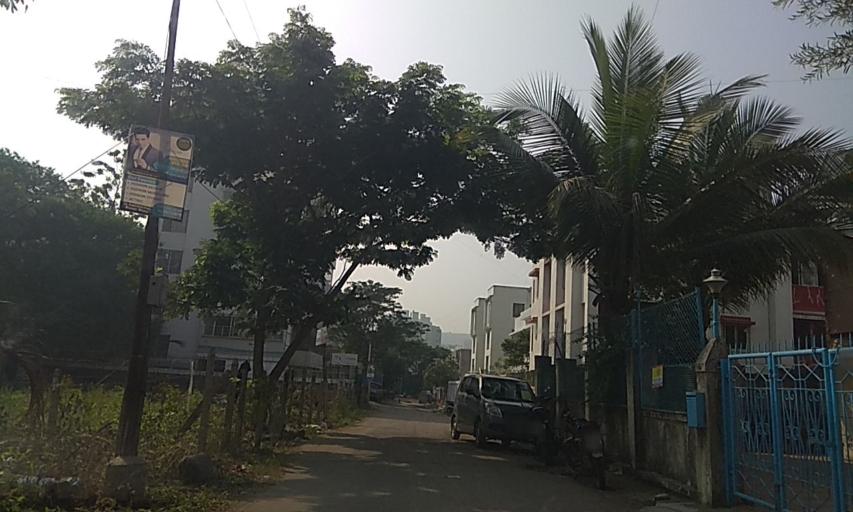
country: IN
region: Maharashtra
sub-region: Pune Division
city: Pimpri
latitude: 18.5628
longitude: 73.7804
